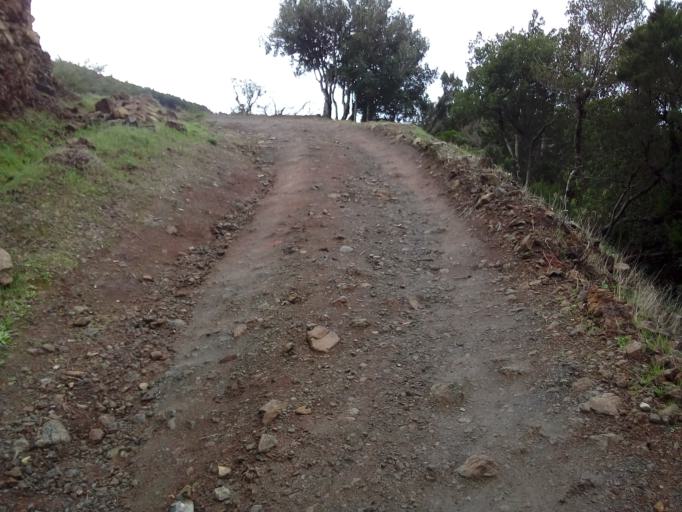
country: ES
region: Canary Islands
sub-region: Provincia de Santa Cruz de Tenerife
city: Vallehermosa
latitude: 28.1376
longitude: -17.2961
